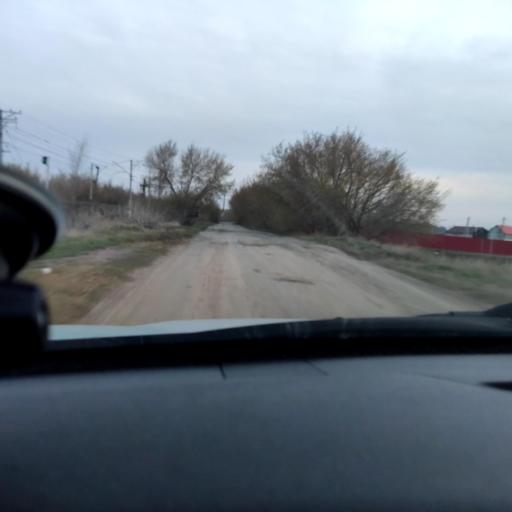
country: RU
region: Samara
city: Smyshlyayevka
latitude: 53.1532
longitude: 50.3912
